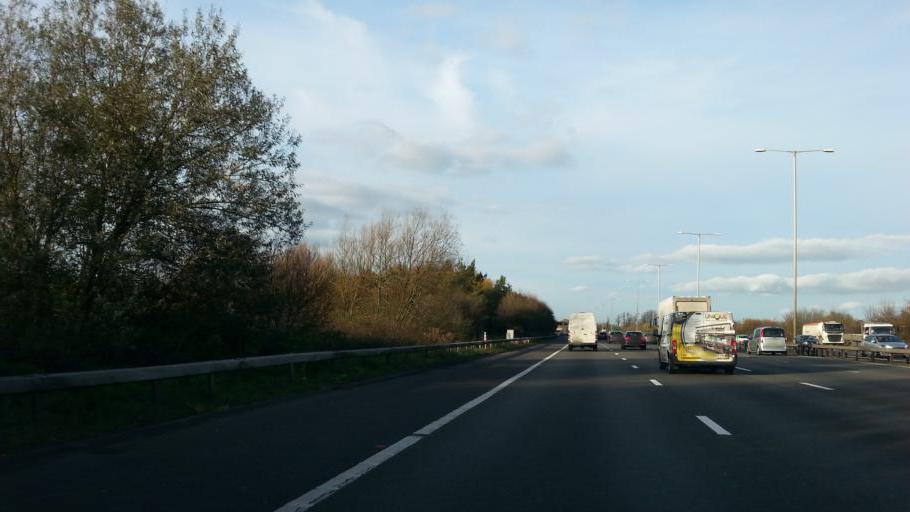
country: GB
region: England
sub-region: Greater London
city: Uxbridge
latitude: 51.5315
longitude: -0.4993
